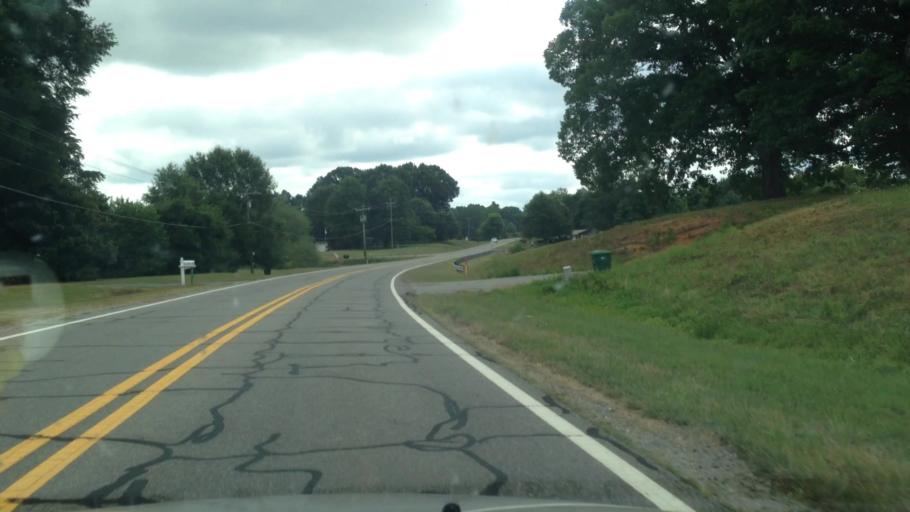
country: US
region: North Carolina
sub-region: Rockingham County
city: Madison
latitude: 36.3803
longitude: -79.9256
